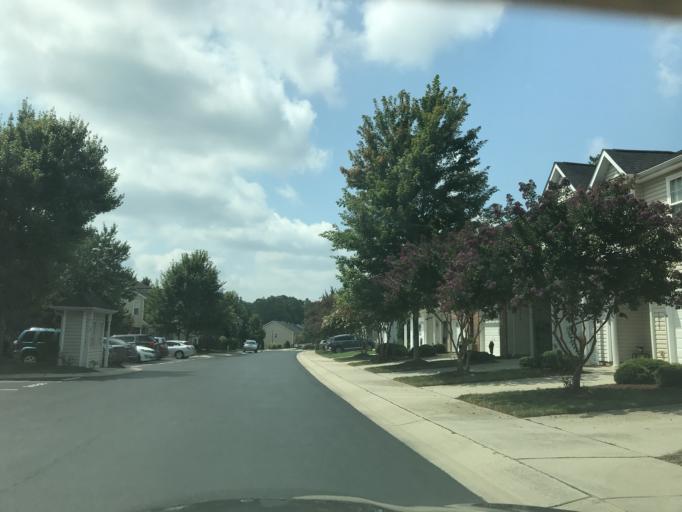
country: US
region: North Carolina
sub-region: Wake County
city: Wake Forest
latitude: 35.9233
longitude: -78.5586
